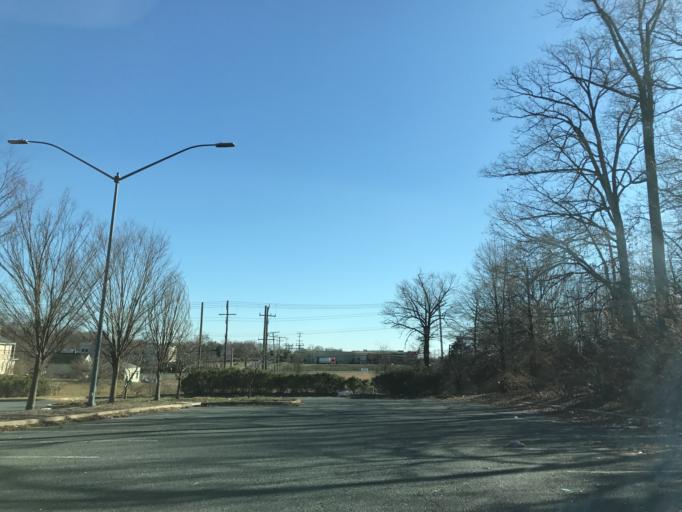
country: US
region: Maryland
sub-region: Harford County
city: Riverside
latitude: 39.4840
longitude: -76.2476
